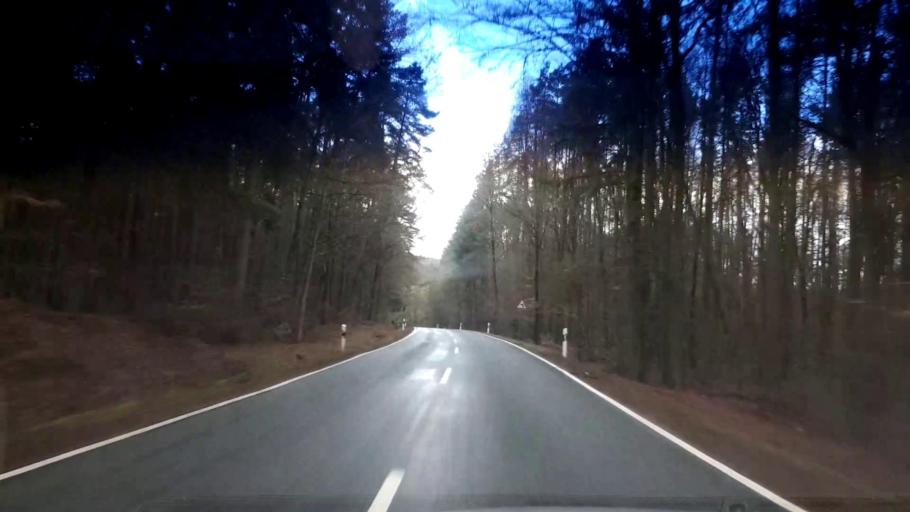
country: DE
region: Bavaria
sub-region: Upper Franconia
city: Lauter
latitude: 49.9656
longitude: 10.7610
